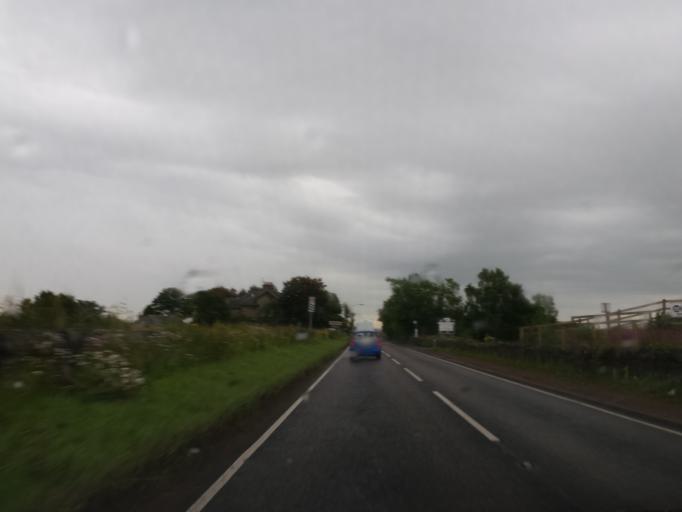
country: GB
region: Scotland
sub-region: Fife
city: Leuchars
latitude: 56.3858
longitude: -2.8941
